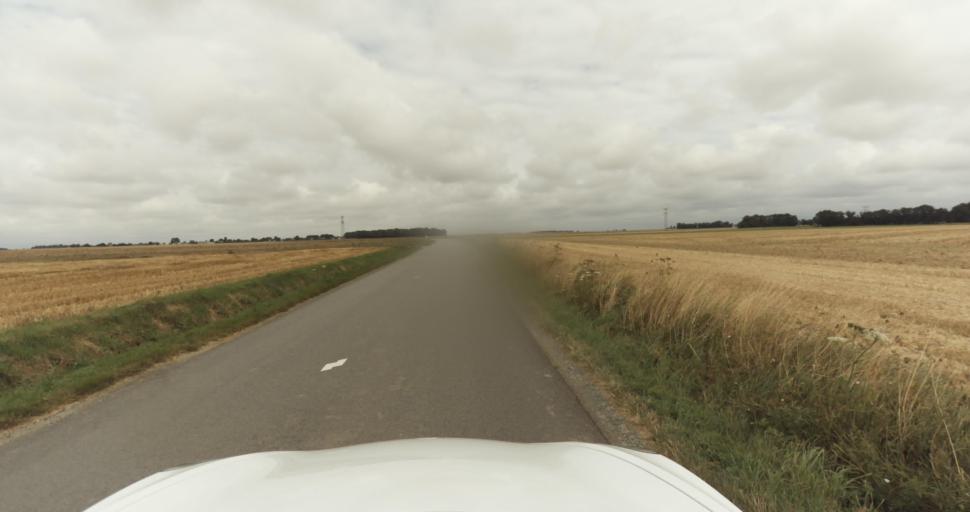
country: FR
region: Haute-Normandie
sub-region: Departement de l'Eure
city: Claville
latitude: 49.0314
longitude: 1.0304
